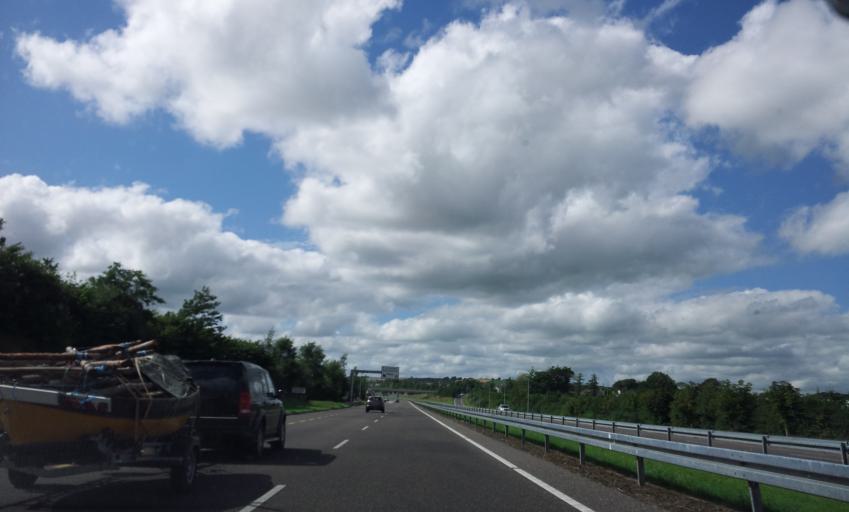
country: IE
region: Munster
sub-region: County Cork
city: Tower
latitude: 51.8747
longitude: -8.6075
